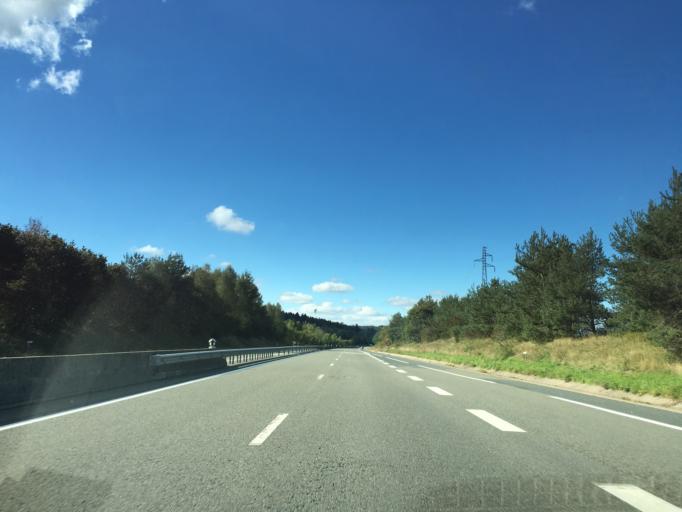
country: FR
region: Lorraine
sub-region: Departement des Vosges
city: Etival-Clairefontaine
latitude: 48.4052
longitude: 6.8169
